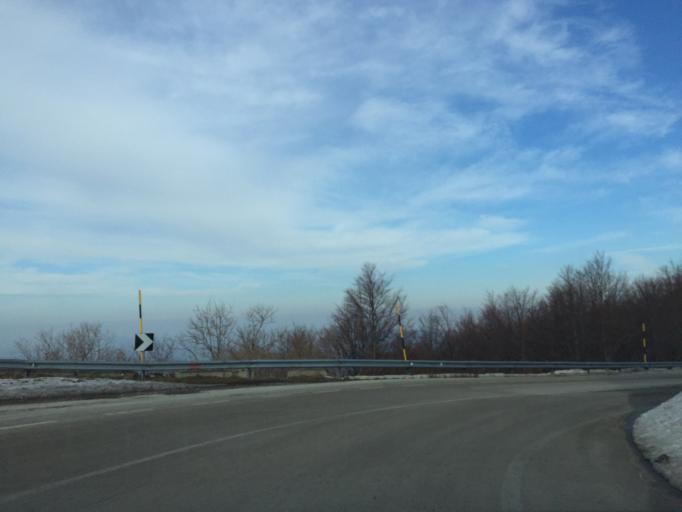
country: IT
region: Molise
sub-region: Provincia di Campobasso
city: San Massimo
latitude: 41.4701
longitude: 14.3949
